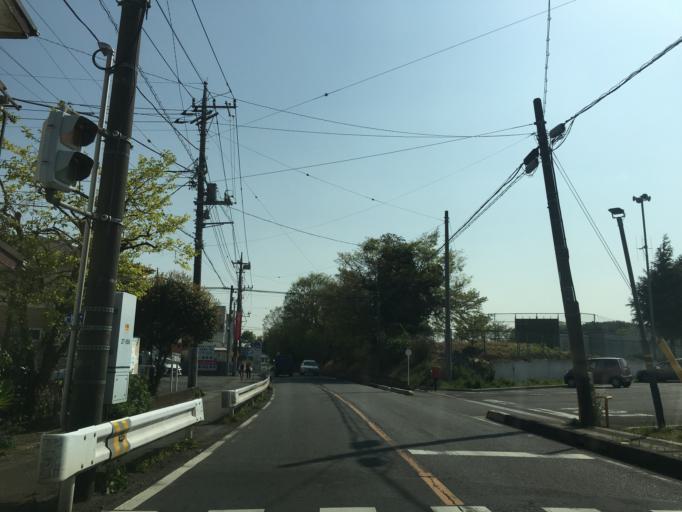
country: JP
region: Saitama
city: Hasuda
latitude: 35.9908
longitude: 139.6734
